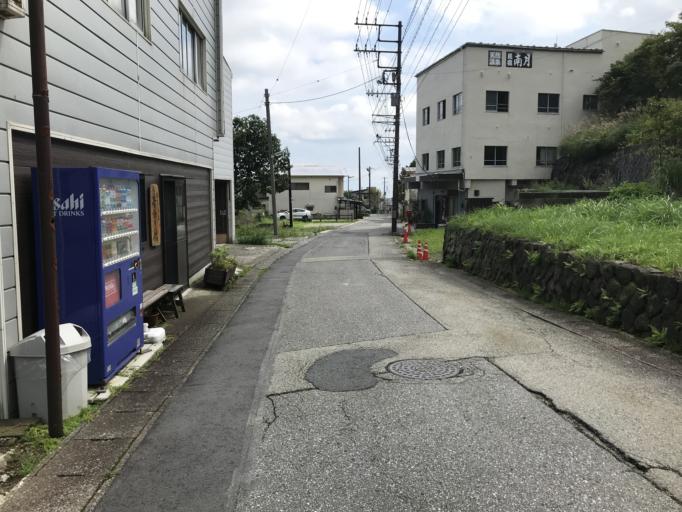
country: JP
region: Tochigi
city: Kuroiso
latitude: 37.0957
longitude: 140.0020
